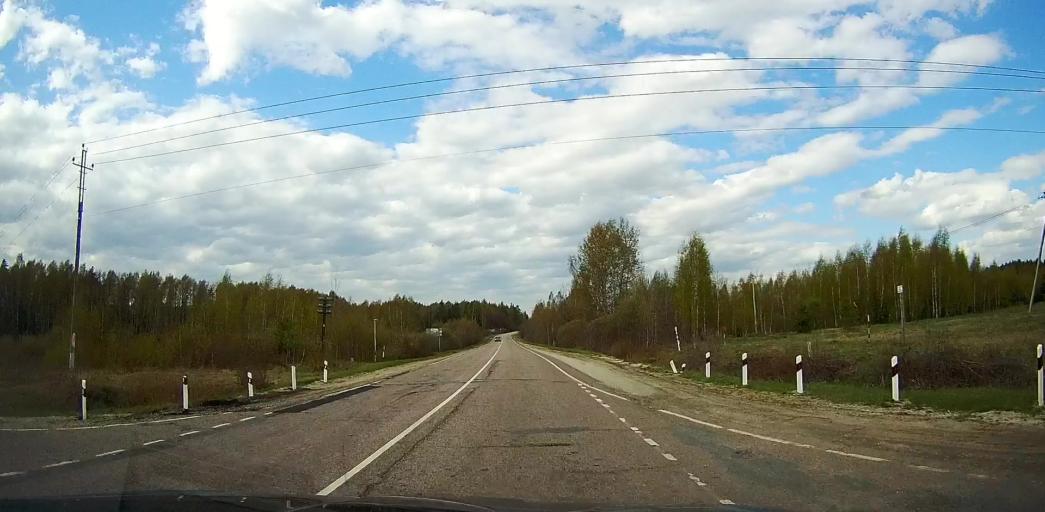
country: RU
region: Moskovskaya
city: Rakhmanovo
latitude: 55.6778
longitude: 38.6444
